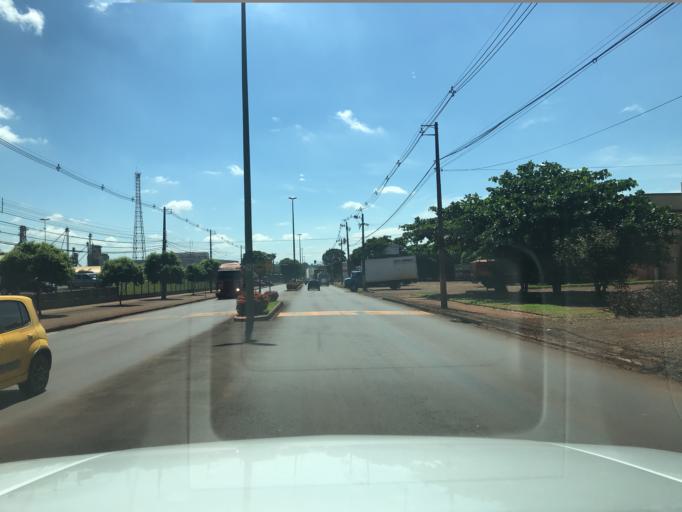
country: BR
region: Parana
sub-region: Palotina
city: Palotina
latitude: -24.2812
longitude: -53.8323
